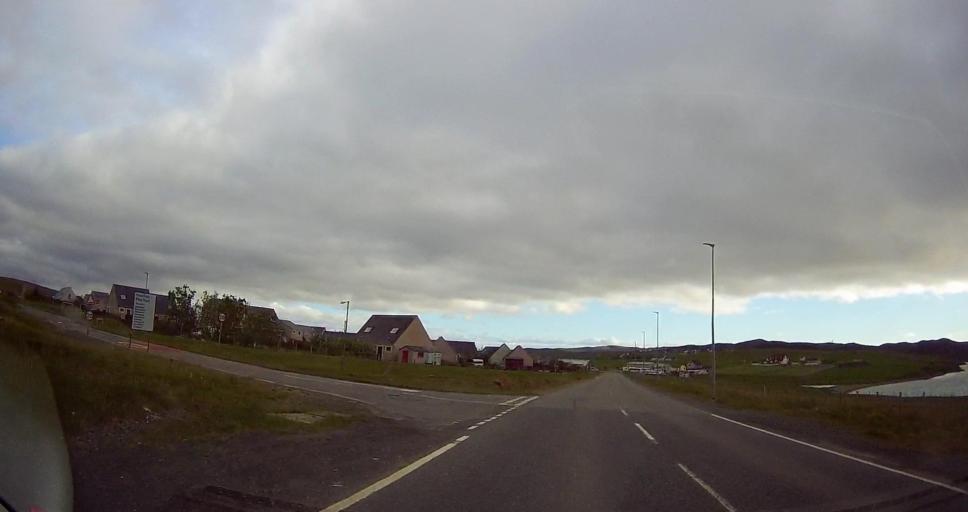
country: GB
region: Scotland
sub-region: Shetland Islands
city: Lerwick
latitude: 60.4011
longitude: -1.3500
